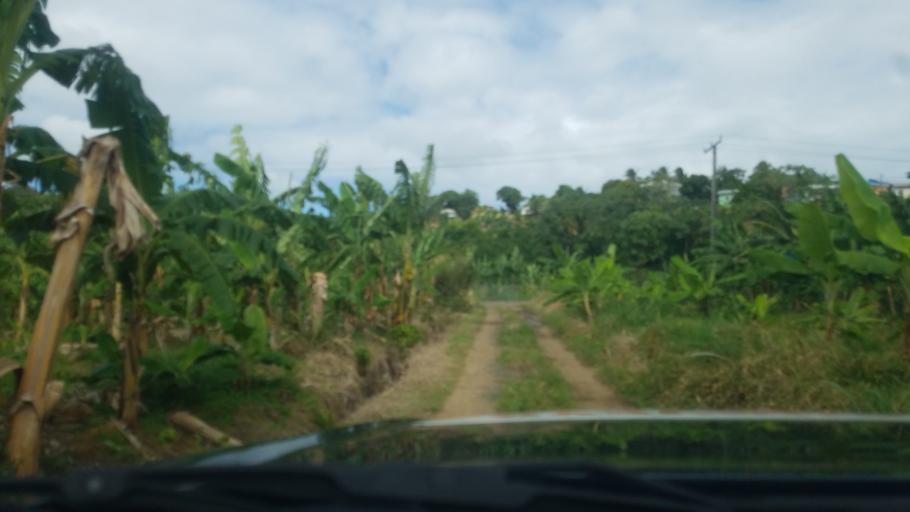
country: LC
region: Dennery Quarter
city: Dennery
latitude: 13.9328
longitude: -60.9252
